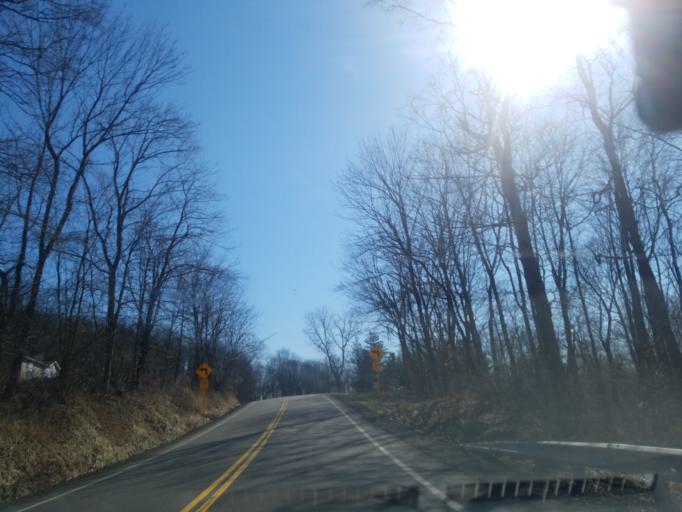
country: US
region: Ohio
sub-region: Tuscarawas County
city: Rockford
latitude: 40.5155
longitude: -81.2757
